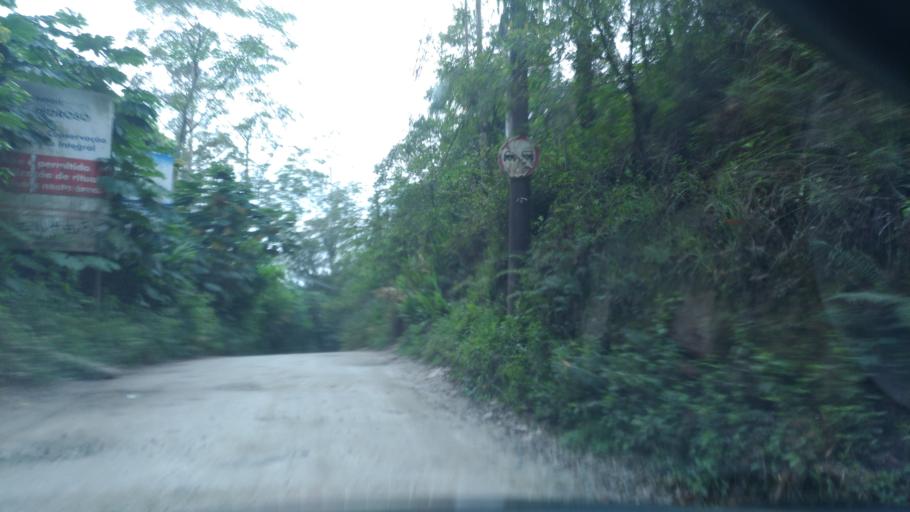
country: BR
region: Sao Paulo
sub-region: Sao Bernardo Do Campo
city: Sao Bernardo do Campo
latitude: -23.7398
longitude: -46.5178
